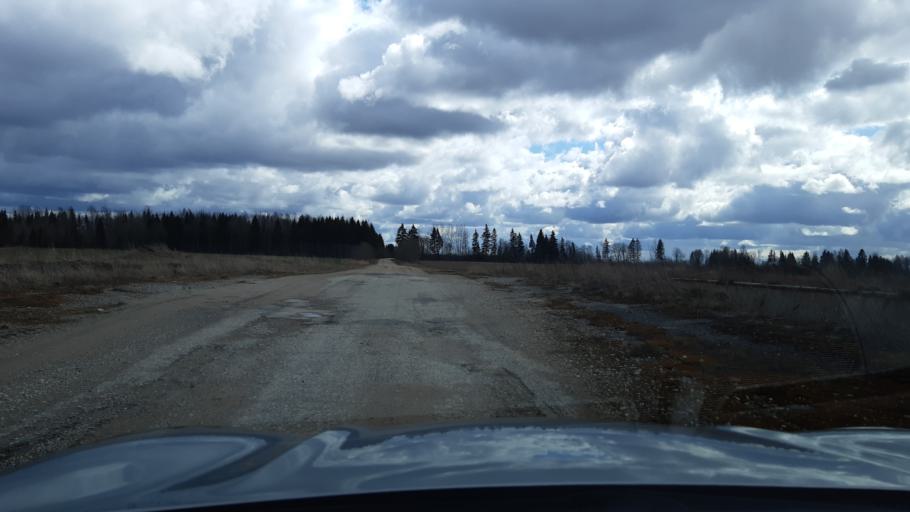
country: EE
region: Harju
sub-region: Rae vald
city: Vaida
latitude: 59.0839
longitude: 25.1412
